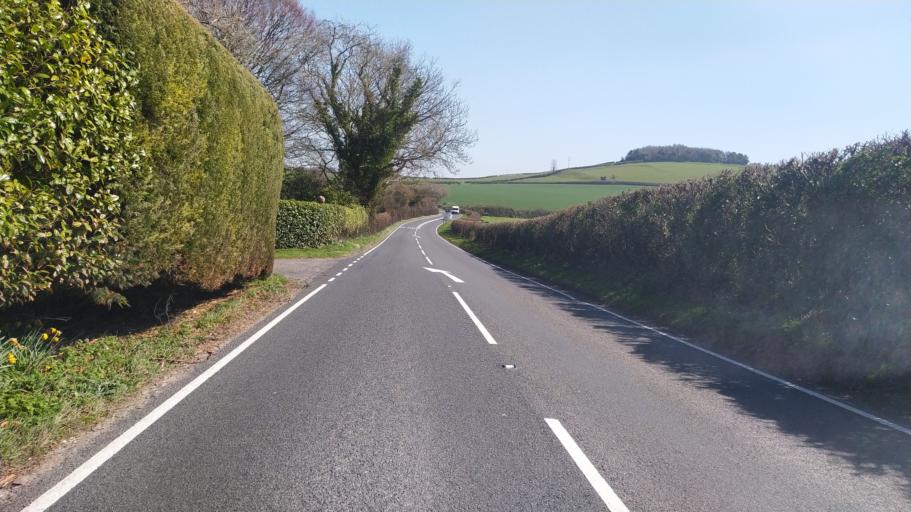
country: GB
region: England
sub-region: Dorset
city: Bovington Camp
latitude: 50.7643
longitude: -2.3249
